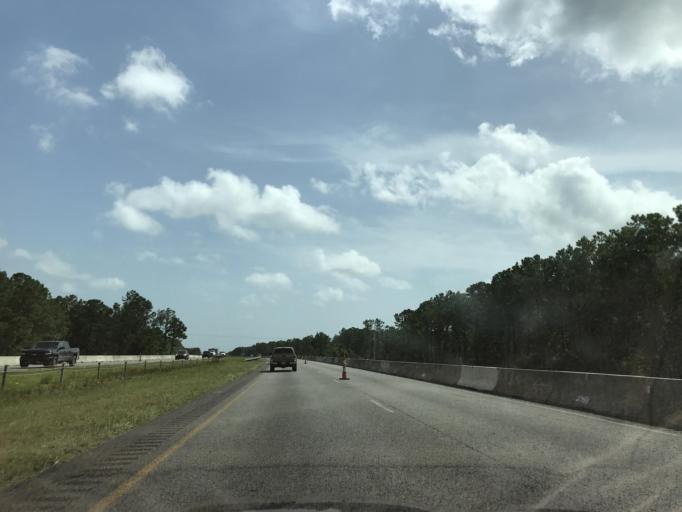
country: US
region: North Carolina
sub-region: New Hanover County
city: Castle Hayne
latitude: 34.3598
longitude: -77.8879
